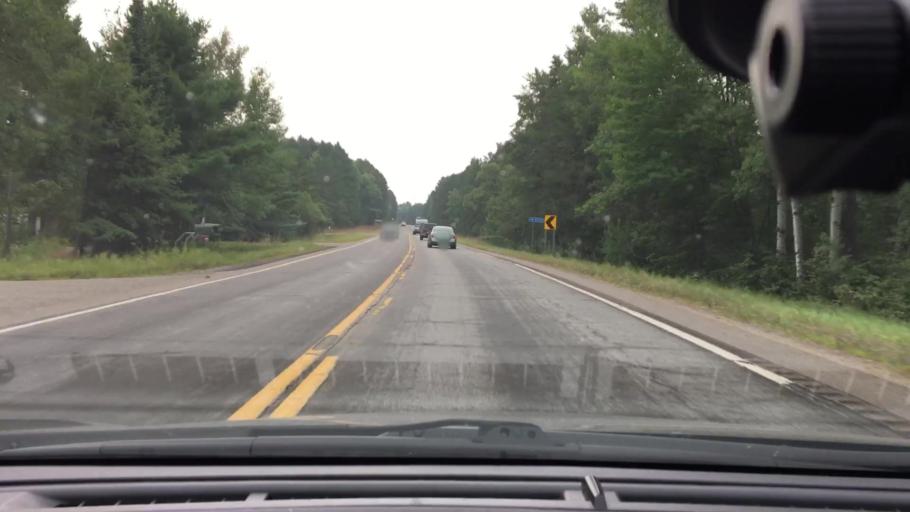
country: US
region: Minnesota
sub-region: Crow Wing County
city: Cross Lake
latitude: 46.7423
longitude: -93.9661
